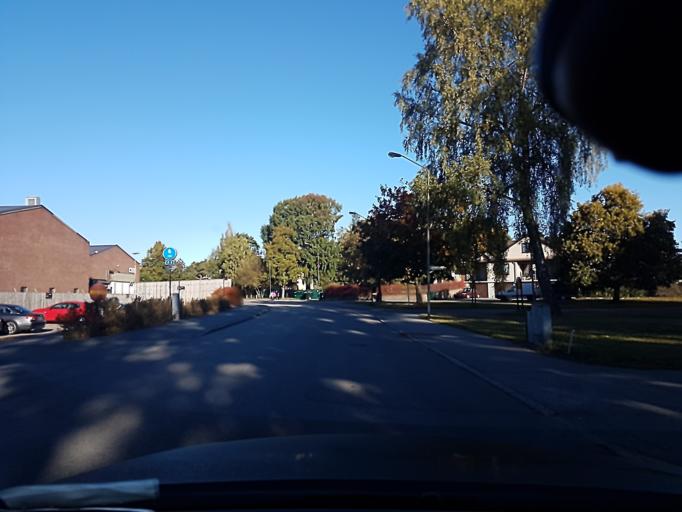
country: SE
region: Kronoberg
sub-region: Vaxjo Kommun
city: Vaexjoe
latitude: 56.8727
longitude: 14.8275
